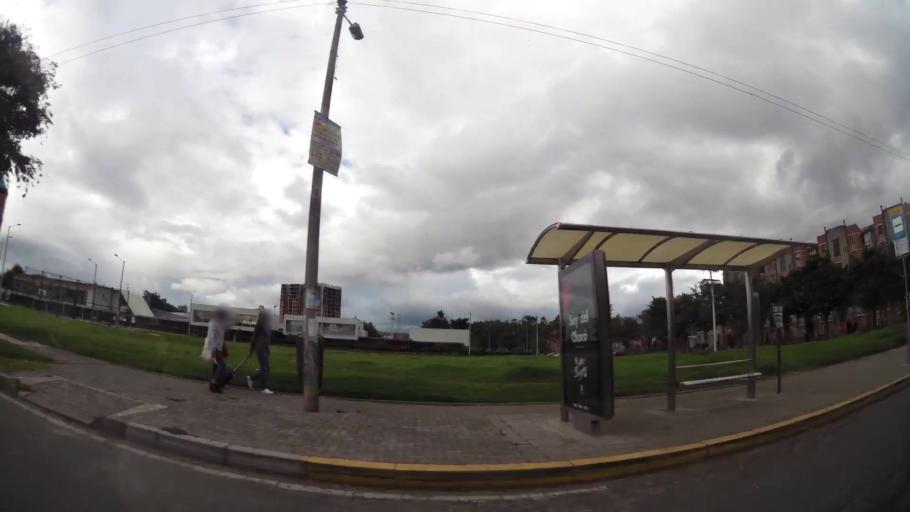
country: CO
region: Cundinamarca
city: Cota
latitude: 4.7190
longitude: -74.1088
